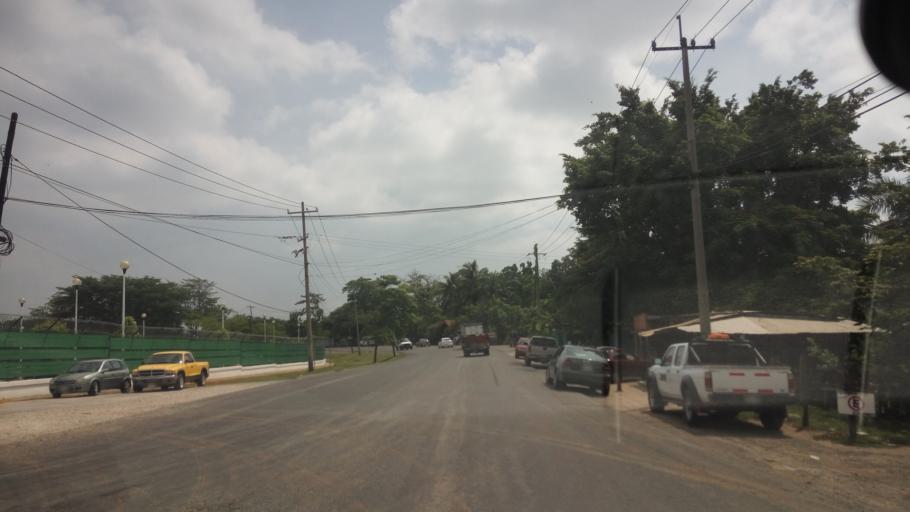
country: MX
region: Chiapas
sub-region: Reforma
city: El Carmen (El Limon)
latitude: 17.8853
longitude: -93.1448
